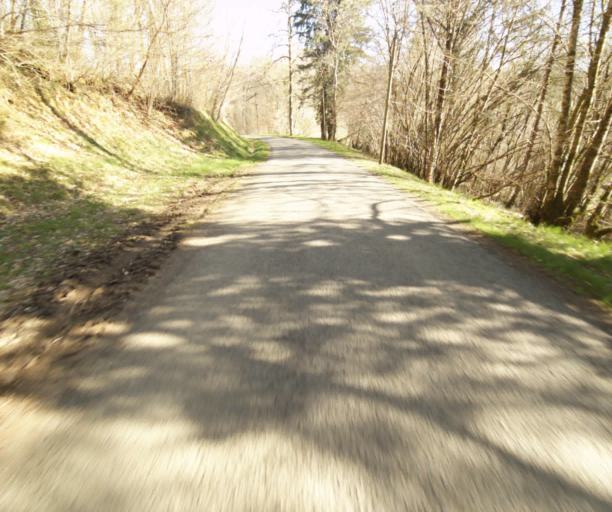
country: FR
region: Limousin
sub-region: Departement de la Correze
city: Seilhac
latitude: 45.3898
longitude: 1.7583
